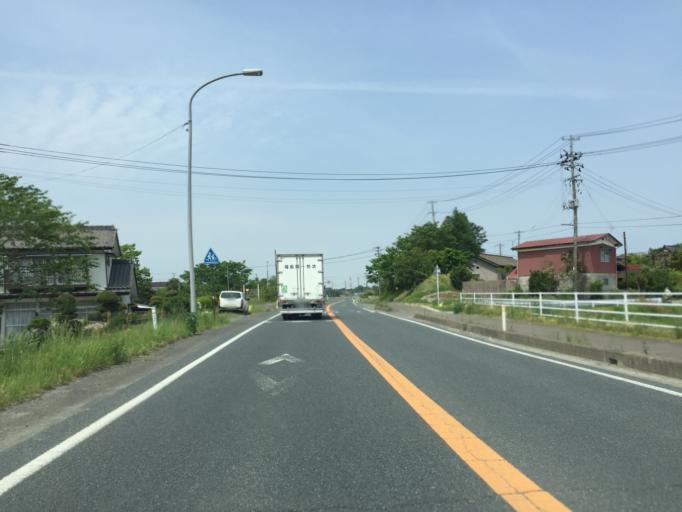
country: JP
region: Miyagi
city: Marumori
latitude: 37.8225
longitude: 140.9198
